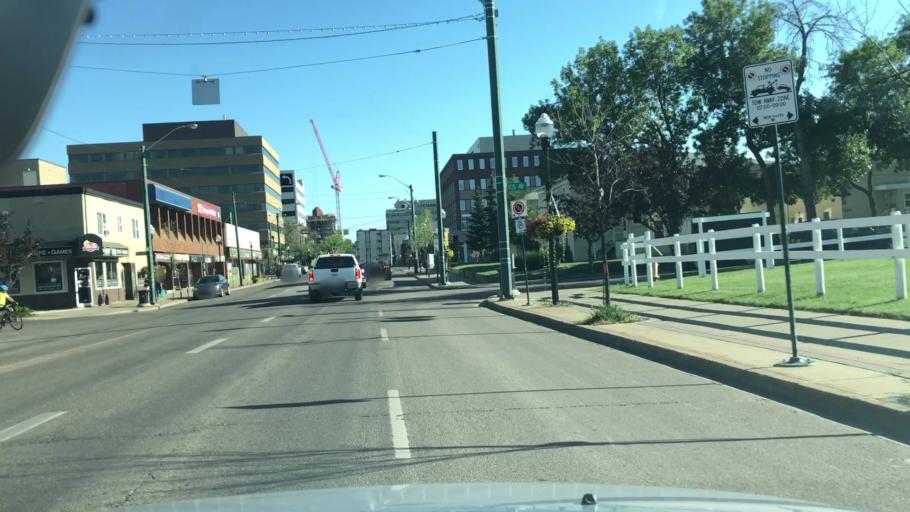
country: CA
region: Alberta
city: Edmonton
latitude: 53.5482
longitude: -113.5359
